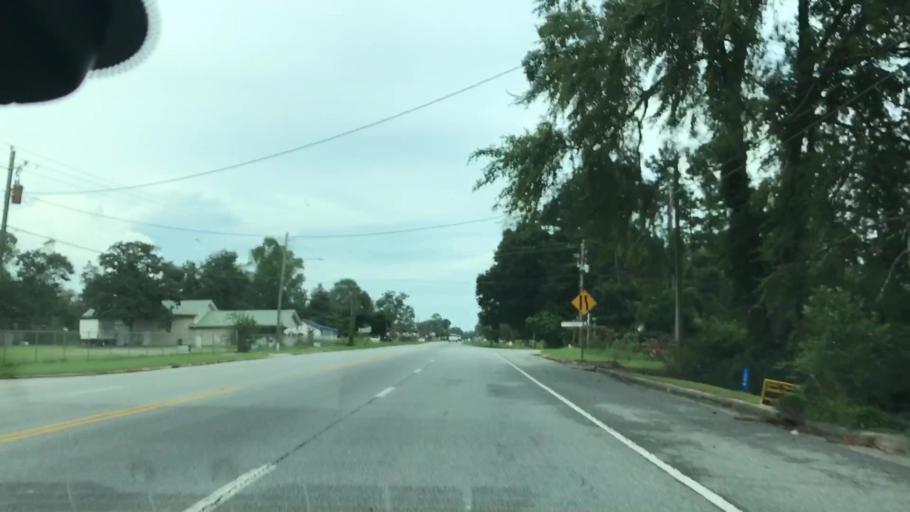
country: US
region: Georgia
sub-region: Quitman County
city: Georgetown
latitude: 31.8843
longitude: -85.0989
